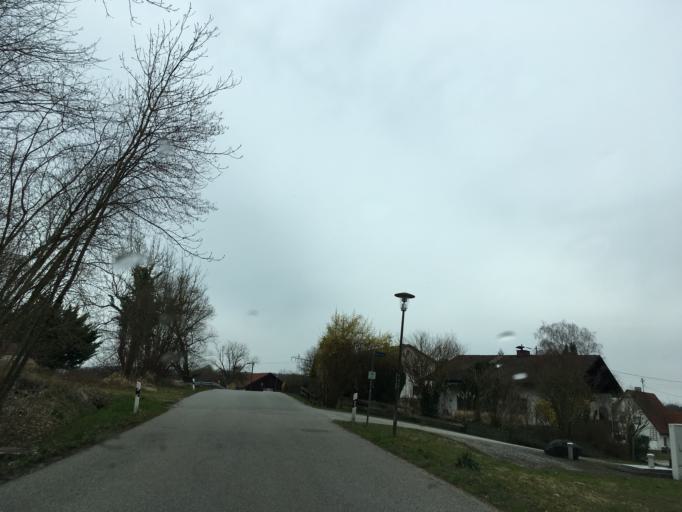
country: DE
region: Bavaria
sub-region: Upper Bavaria
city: Jettenbach
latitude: 48.1707
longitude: 12.3833
